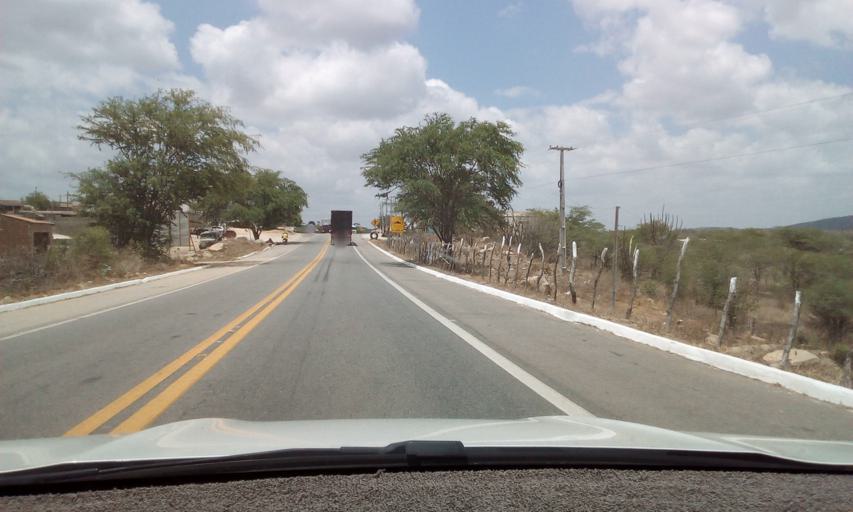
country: BR
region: Pernambuco
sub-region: Taquaritinga Do Norte
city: Taquaritinga do Norte
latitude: -7.7361
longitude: -36.0783
